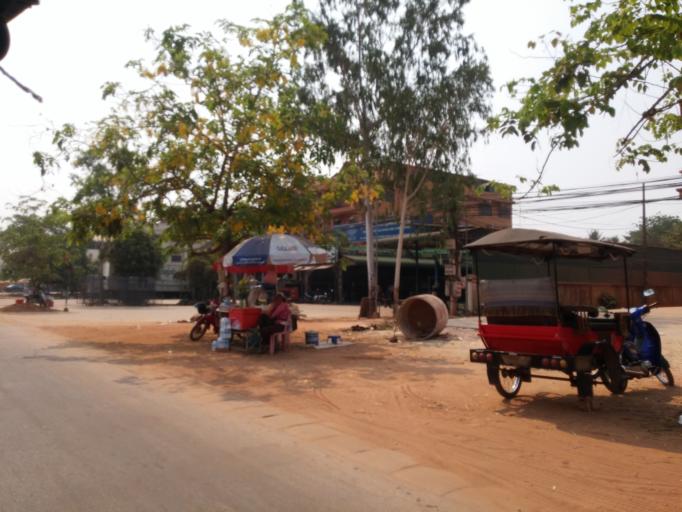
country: KH
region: Siem Reap
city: Siem Reap
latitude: 13.3588
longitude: 103.8845
